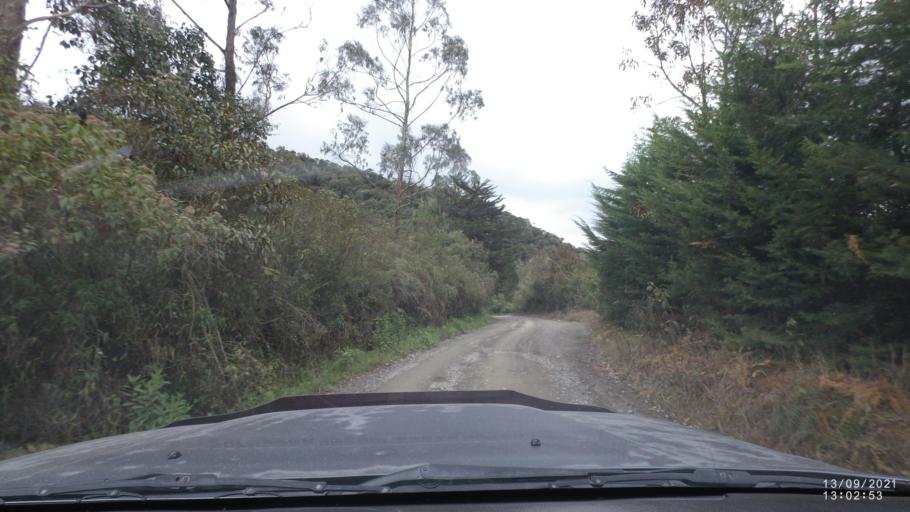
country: BO
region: Cochabamba
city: Colomi
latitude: -17.2288
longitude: -65.8176
